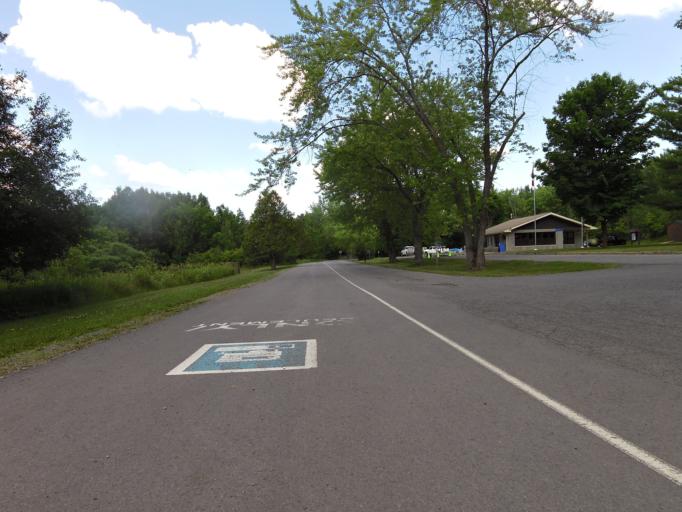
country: CA
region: Ontario
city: Arnprior
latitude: 45.4815
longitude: -76.2134
